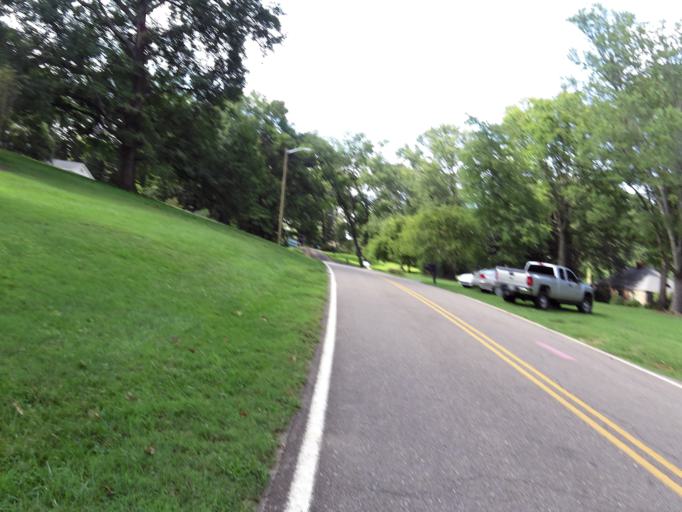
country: US
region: Tennessee
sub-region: Knox County
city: Knoxville
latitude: 35.9292
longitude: -83.9612
